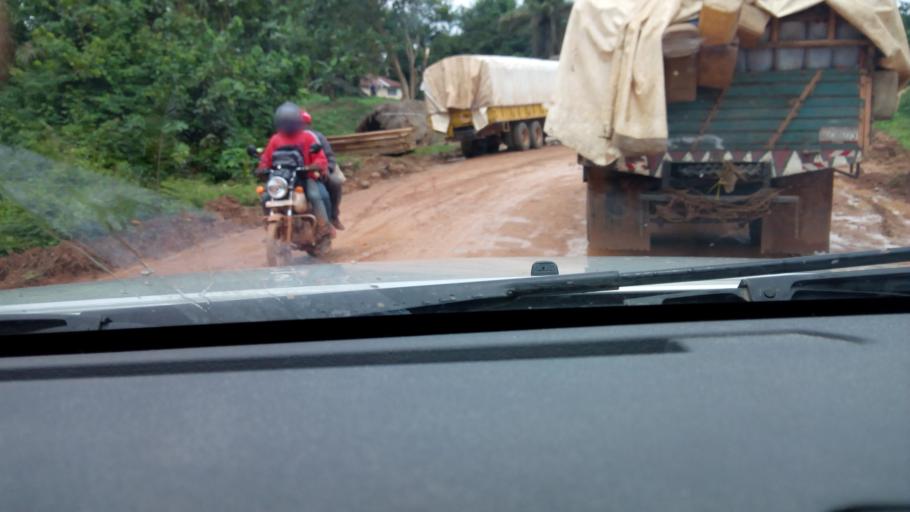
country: CI
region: Dix-Huit Montagnes
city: Toulepleu Guere
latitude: 6.8263
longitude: -8.8110
